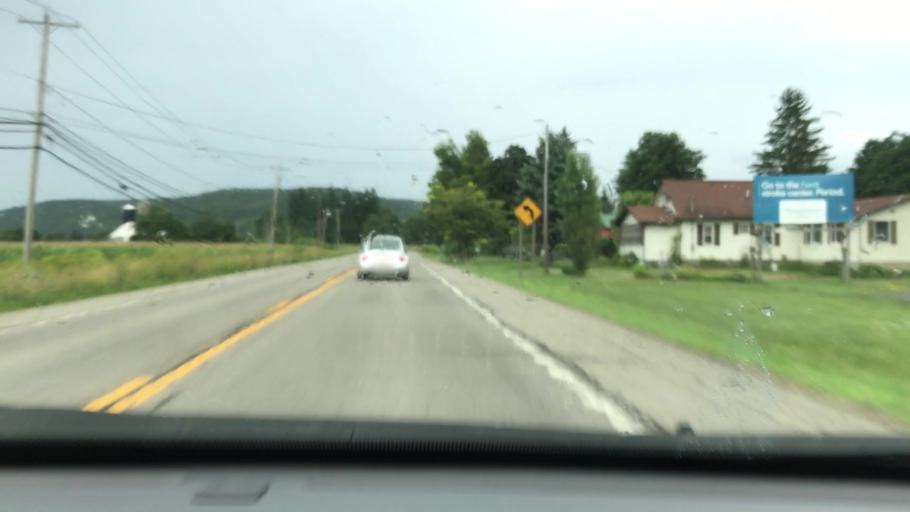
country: US
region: New York
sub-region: Cattaraugus County
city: Salamanca
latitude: 42.1959
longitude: -78.6548
